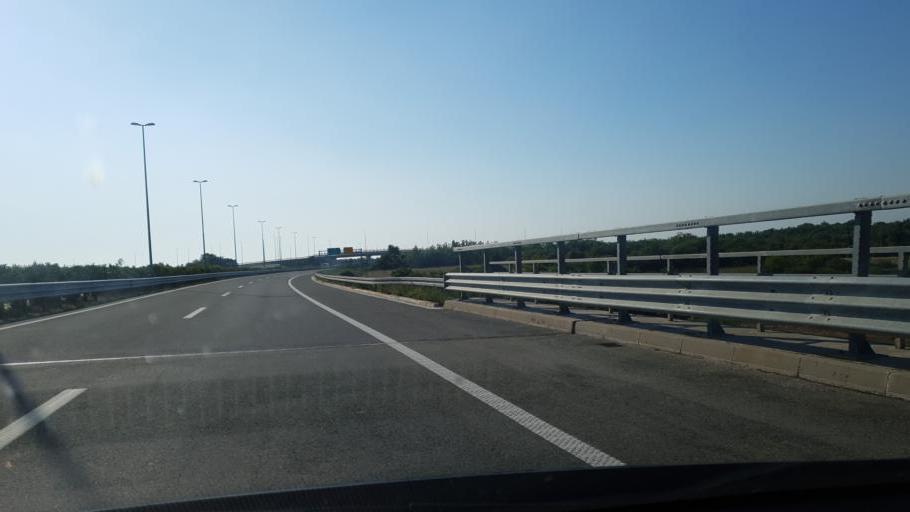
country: HR
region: Istarska
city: Vodnjan
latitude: 44.9845
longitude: 13.8510
